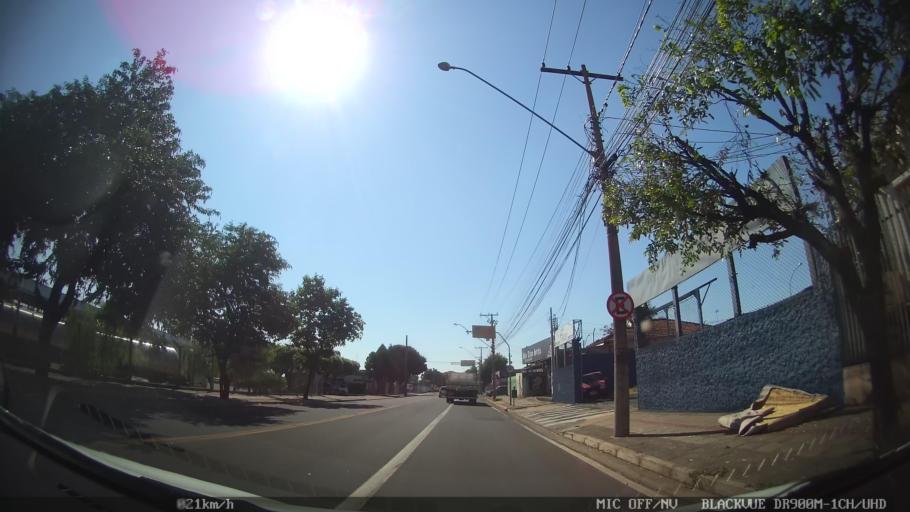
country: BR
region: Sao Paulo
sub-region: Sao Jose Do Rio Preto
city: Sao Jose do Rio Preto
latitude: -20.7947
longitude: -49.3901
